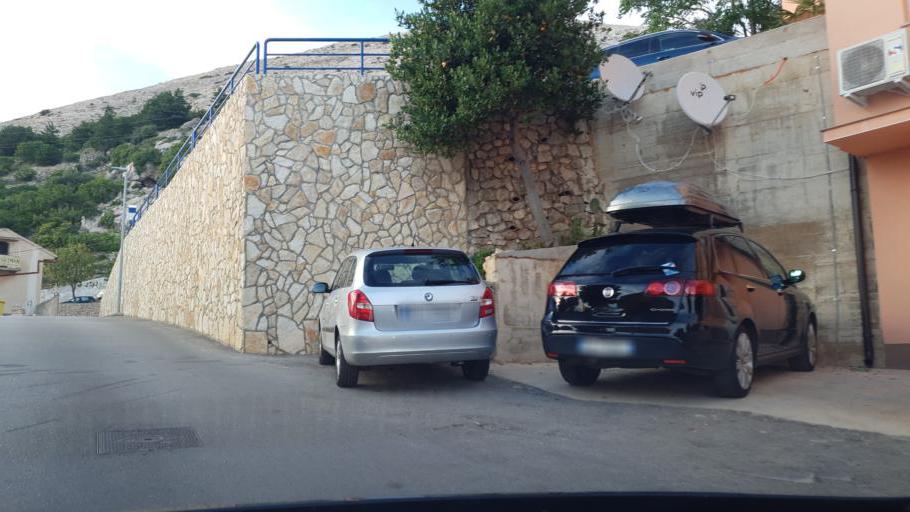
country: HR
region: Primorsko-Goranska
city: Punat
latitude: 44.9604
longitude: 14.6863
